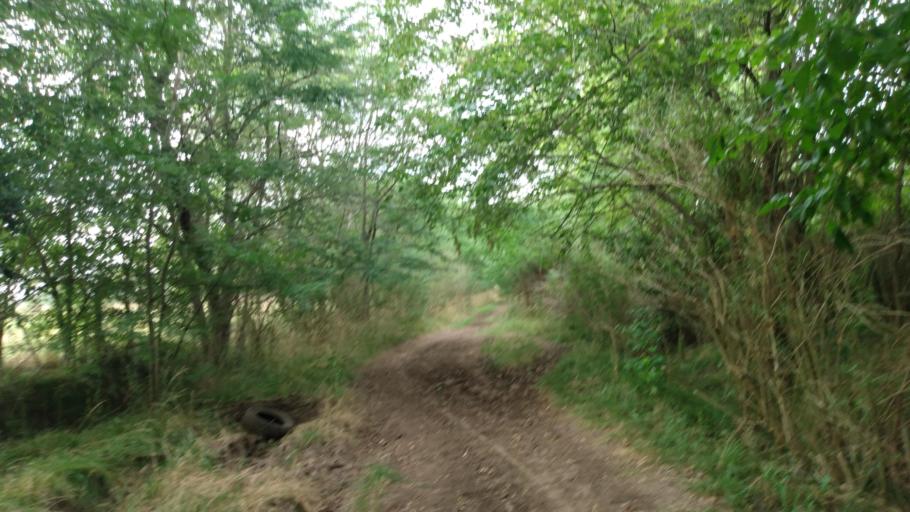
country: AR
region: Buenos Aires
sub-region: Partido de Lujan
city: Lujan
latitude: -34.6001
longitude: -59.0625
